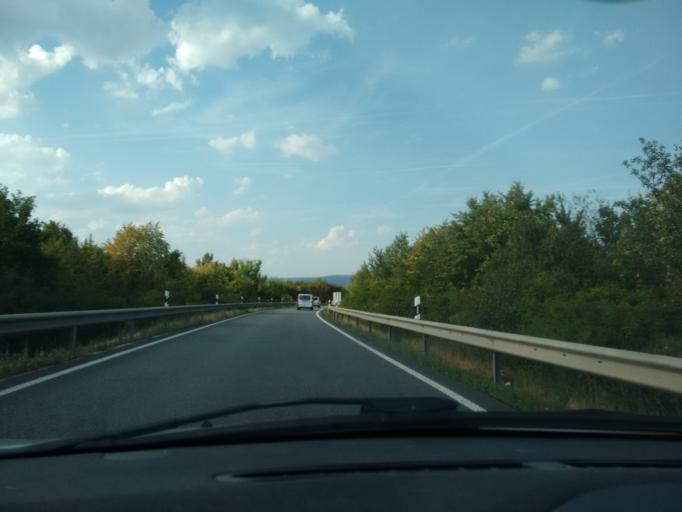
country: DE
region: Rheinland-Pfalz
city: Gensingen
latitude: 49.9304
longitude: 7.9414
